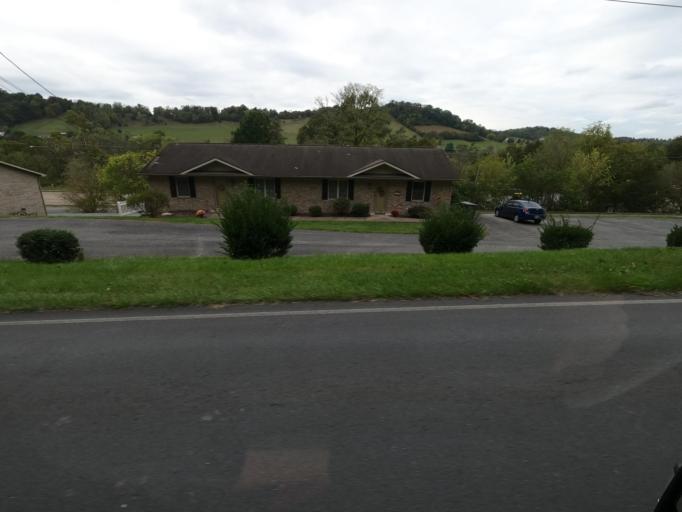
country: US
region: Tennessee
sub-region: Carter County
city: Central
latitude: 36.3391
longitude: -82.2568
